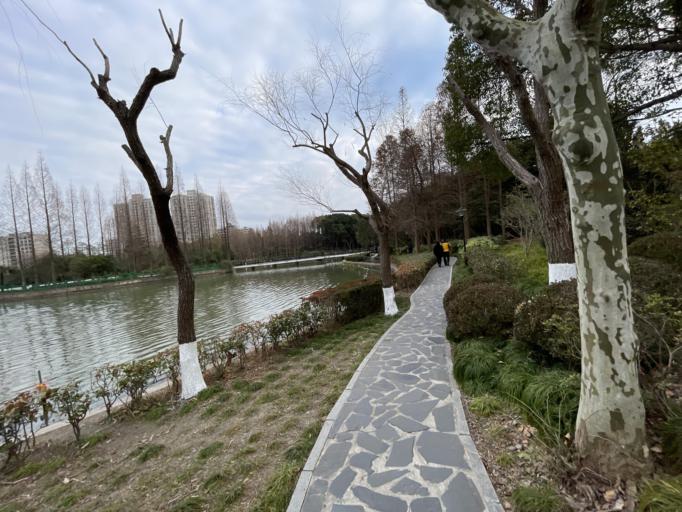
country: CN
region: Shanghai Shi
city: Yangpu
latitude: 31.2937
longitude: 121.5234
